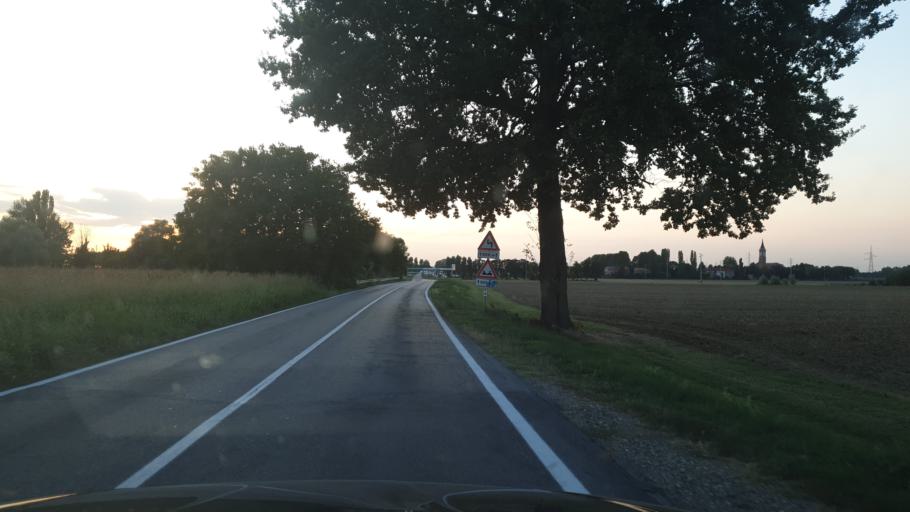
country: IT
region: Emilia-Romagna
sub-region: Provincia di Bologna
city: Progresso
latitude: 44.5660
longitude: 11.3978
